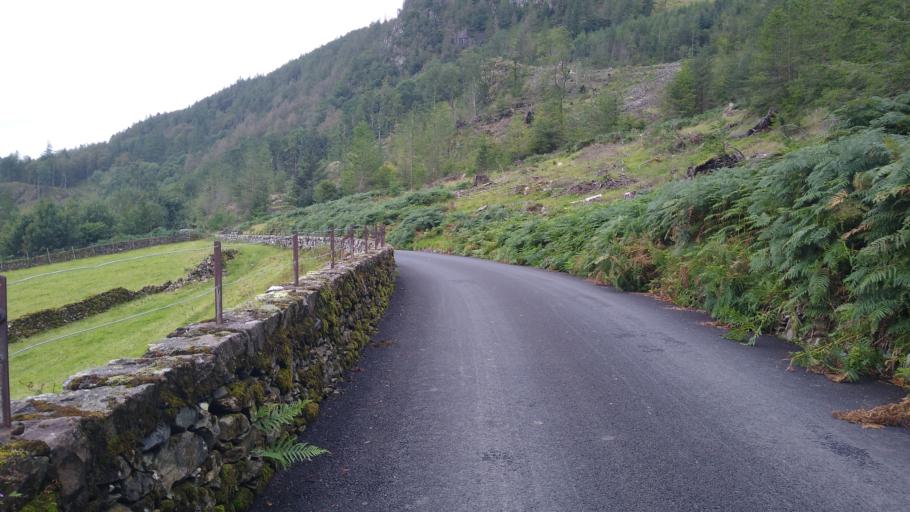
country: GB
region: England
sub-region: Cumbria
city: Keswick
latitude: 54.5632
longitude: -3.0725
